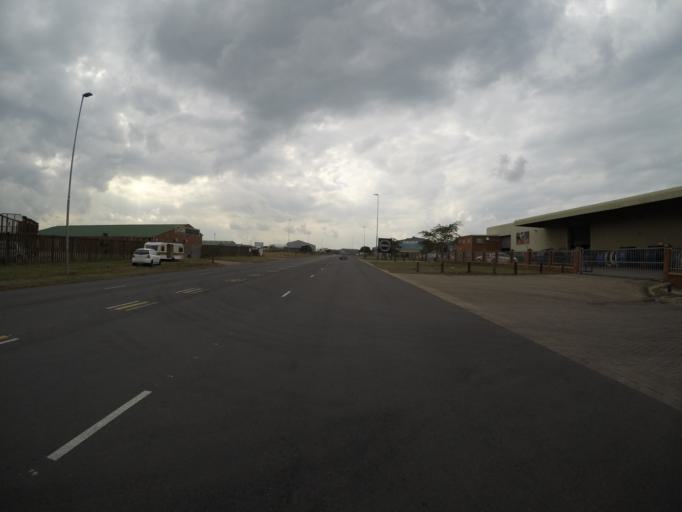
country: ZA
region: KwaZulu-Natal
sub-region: uThungulu District Municipality
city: Richards Bay
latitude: -28.7407
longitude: 32.0361
